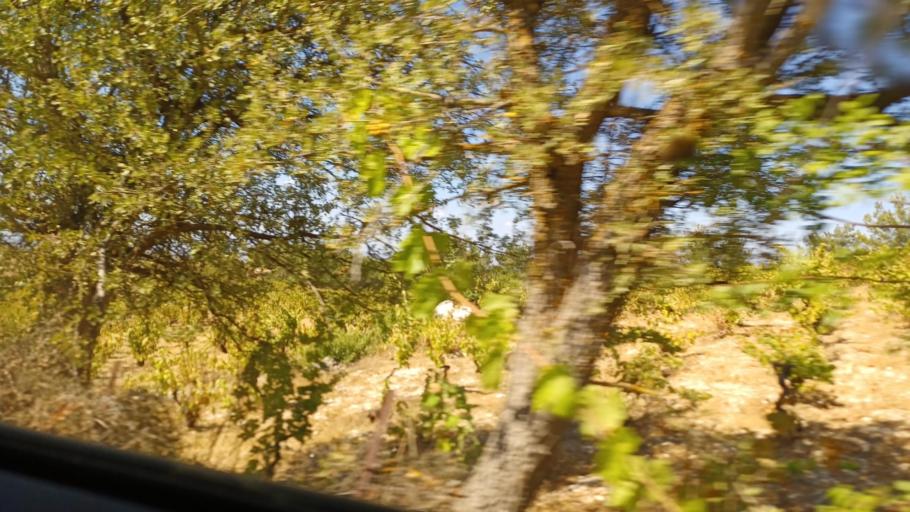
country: CY
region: Pafos
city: Mesogi
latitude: 34.9075
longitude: 32.6207
